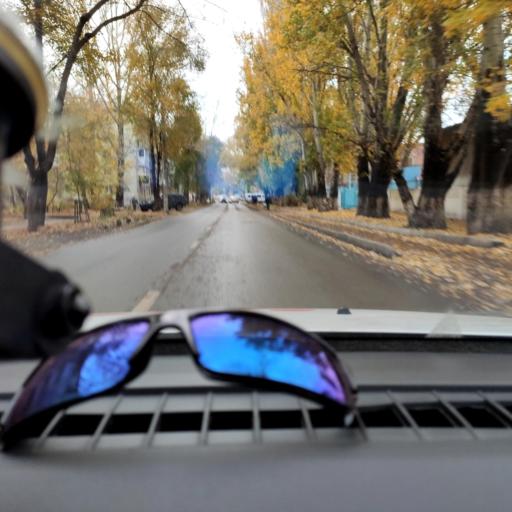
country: RU
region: Samara
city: Samara
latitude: 53.1951
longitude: 50.1838
